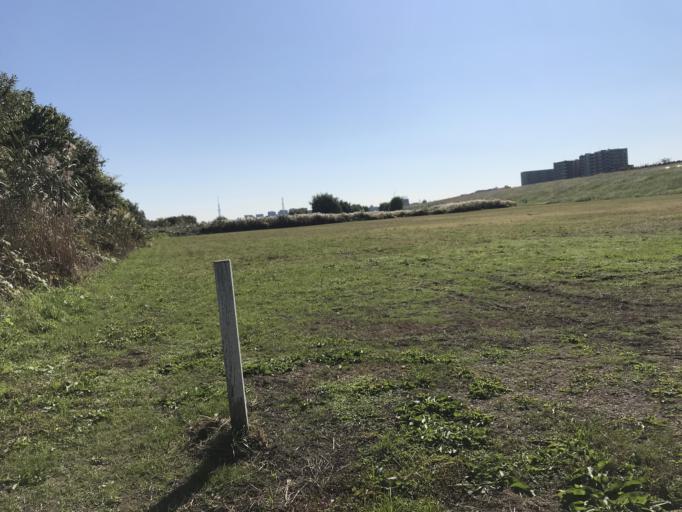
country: JP
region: Saitama
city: Kawaguchi
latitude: 35.7870
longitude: 139.7358
